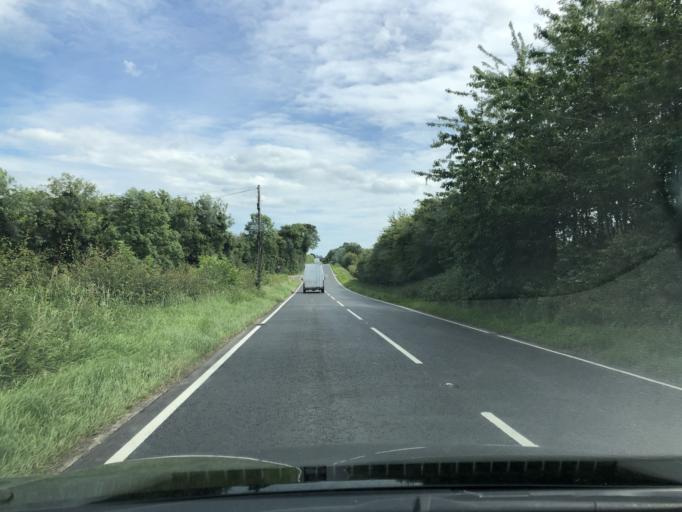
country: GB
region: Northern Ireland
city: Annahilt
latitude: 54.4458
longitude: -5.9479
